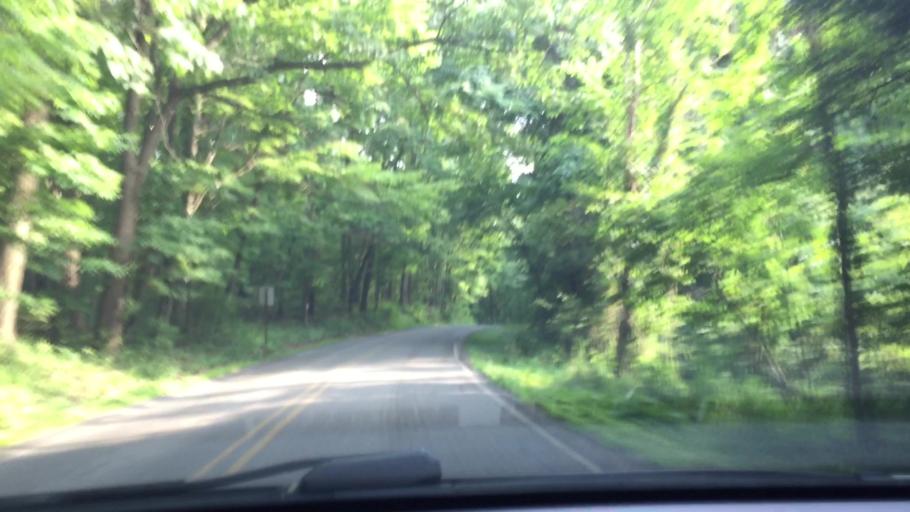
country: US
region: Pennsylvania
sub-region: Butler County
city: Seven Fields
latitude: 40.6672
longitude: -80.0728
